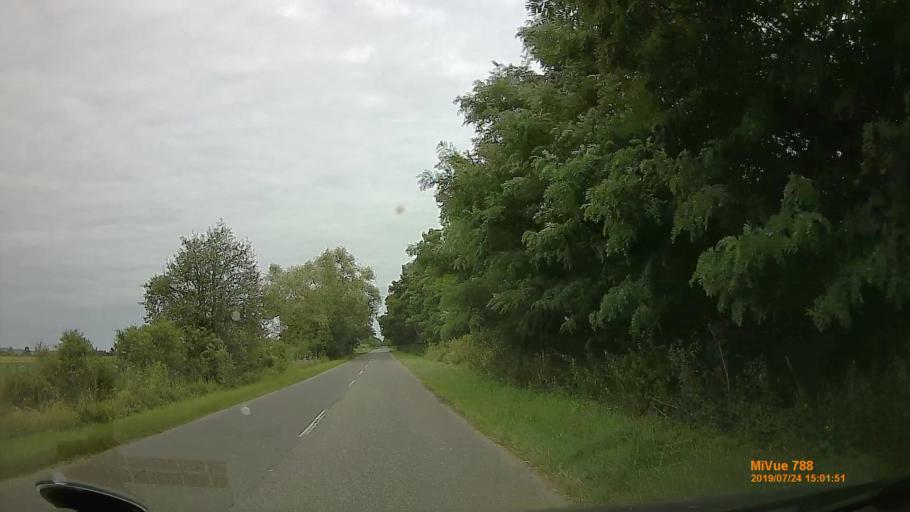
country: HU
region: Szabolcs-Szatmar-Bereg
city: Vasarosnameny
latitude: 48.2270
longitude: 22.3966
